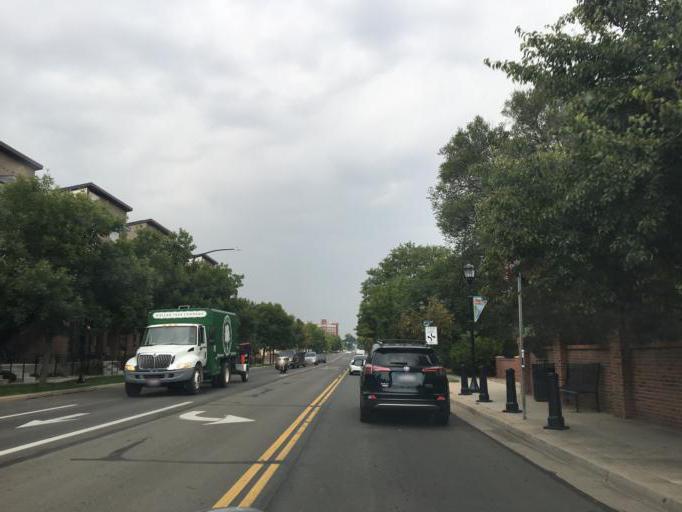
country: US
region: Colorado
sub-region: Jefferson County
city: Edgewater
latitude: 39.7694
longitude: -105.0583
